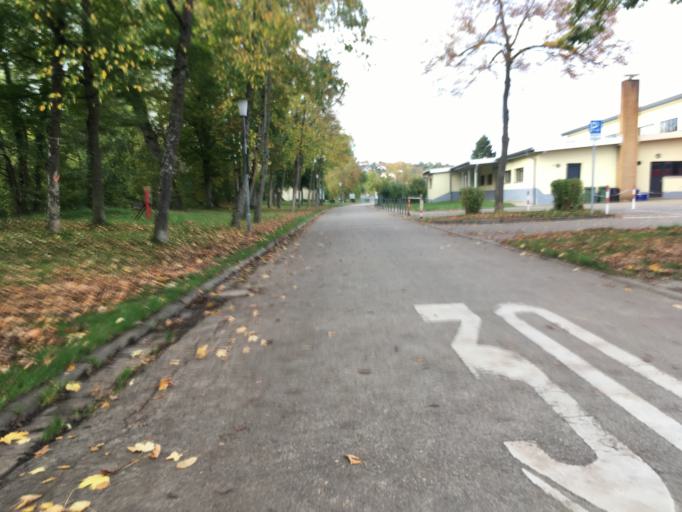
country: DE
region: Baden-Wuerttemberg
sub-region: Regierungsbezirk Stuttgart
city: Ittlingen
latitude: 49.2141
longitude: 8.9205
